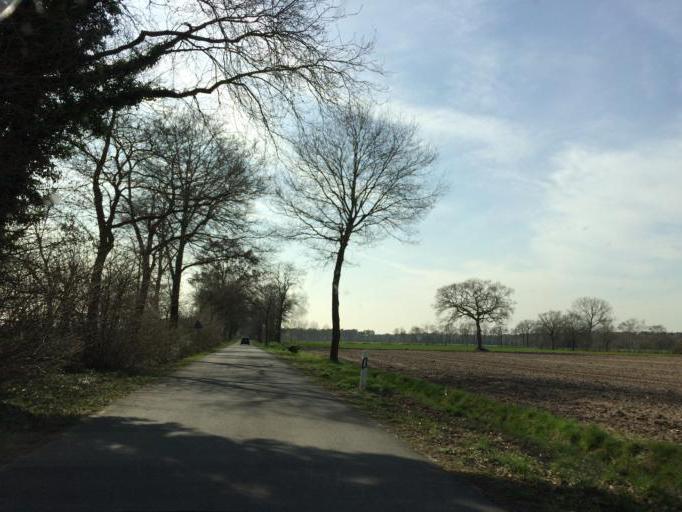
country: DE
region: North Rhine-Westphalia
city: Marl
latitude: 51.7149
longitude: 7.0772
